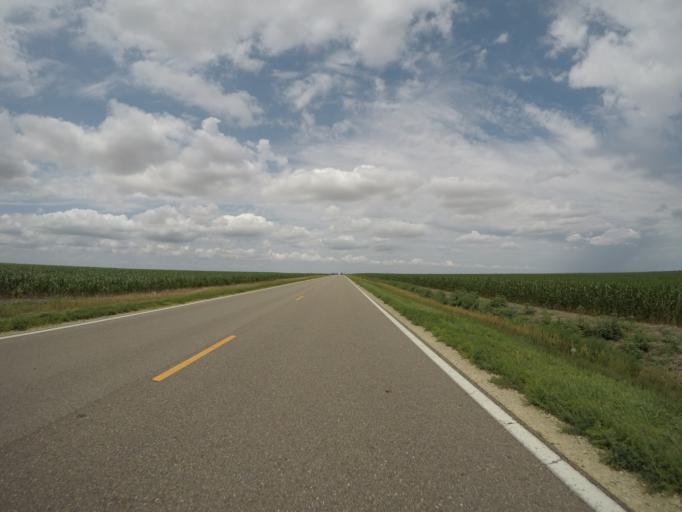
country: US
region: Kansas
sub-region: Rawlins County
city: Atwood
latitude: 39.6710
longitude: -101.0566
